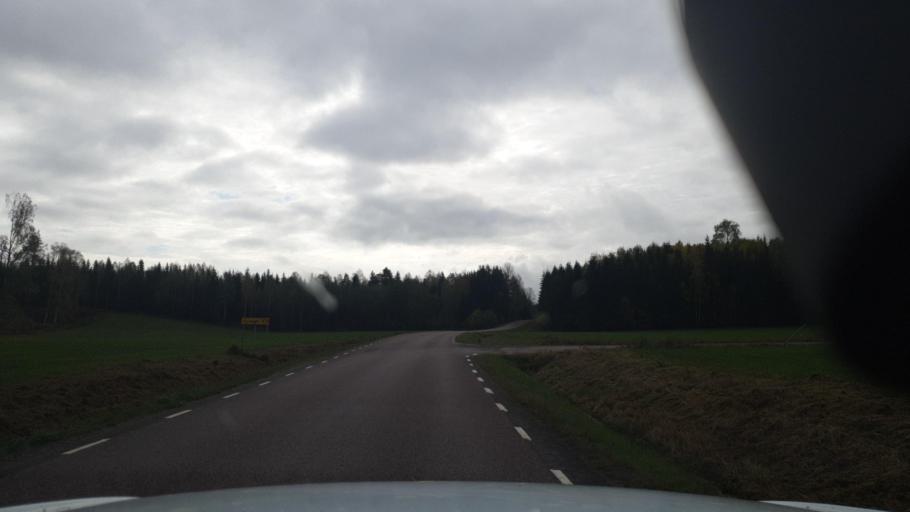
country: SE
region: Vaermland
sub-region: Karlstads Kommun
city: Edsvalla
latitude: 59.5229
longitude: 13.1123
